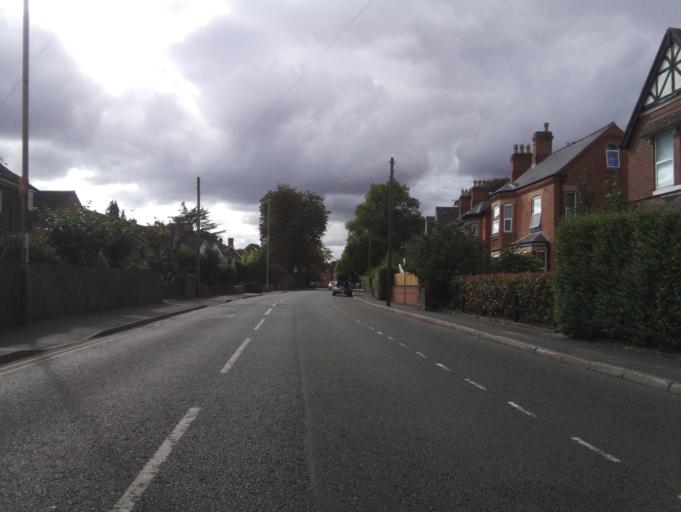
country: GB
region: England
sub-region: Leicestershire
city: Loughborough
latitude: 52.7723
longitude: -1.2174
